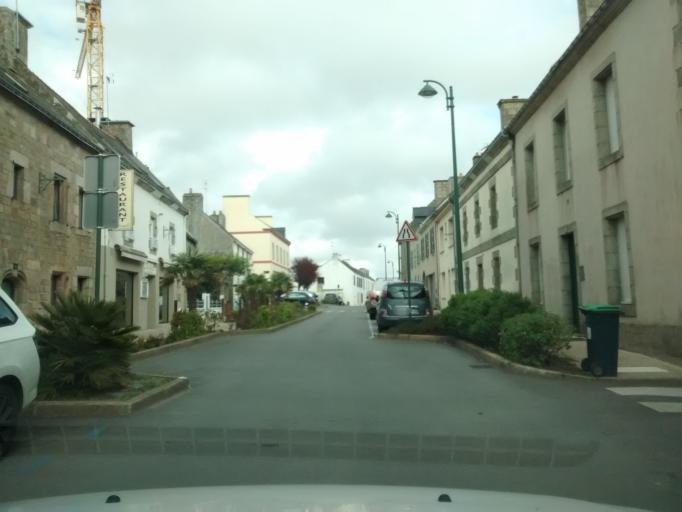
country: FR
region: Brittany
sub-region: Departement du Morbihan
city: Guidel-Plage
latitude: 47.7893
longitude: -3.4872
